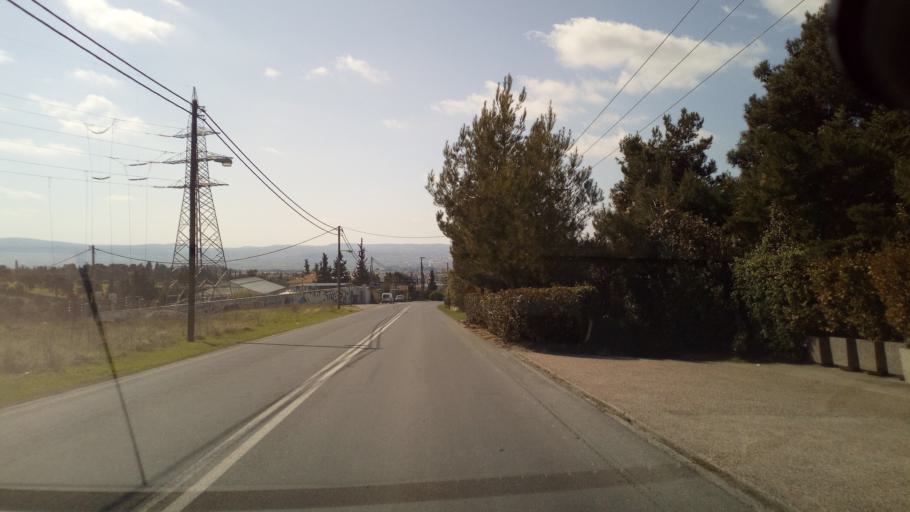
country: GR
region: Central Macedonia
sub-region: Nomos Thessalonikis
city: Thermi
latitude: 40.5647
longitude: 23.0249
